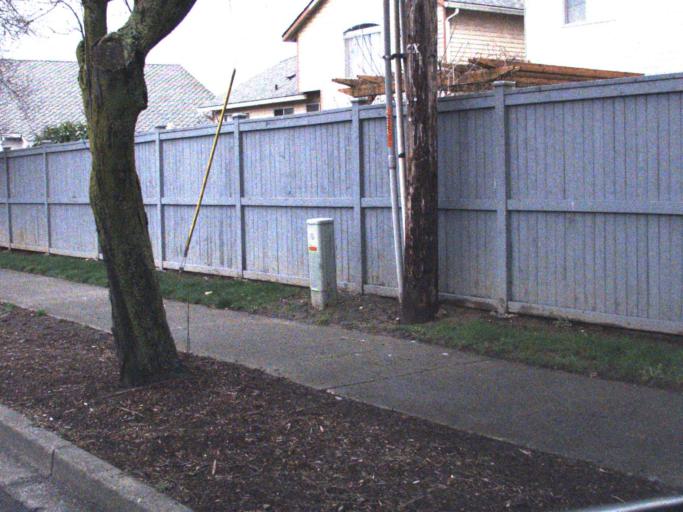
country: US
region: Washington
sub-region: Snohomish County
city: Marysville
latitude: 48.0539
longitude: -122.1547
